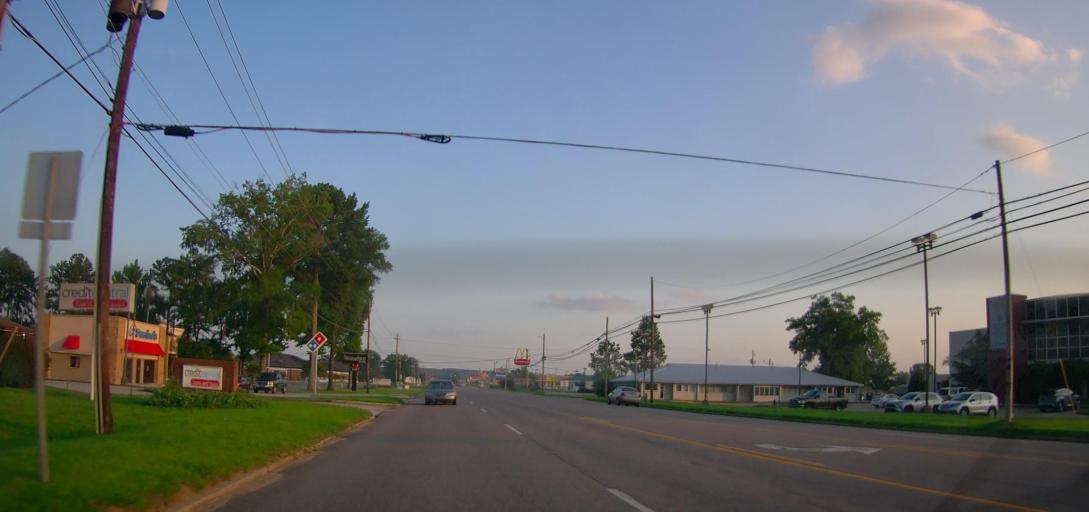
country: US
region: Alabama
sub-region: Marion County
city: Hamilton
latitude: 34.1264
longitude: -87.9898
